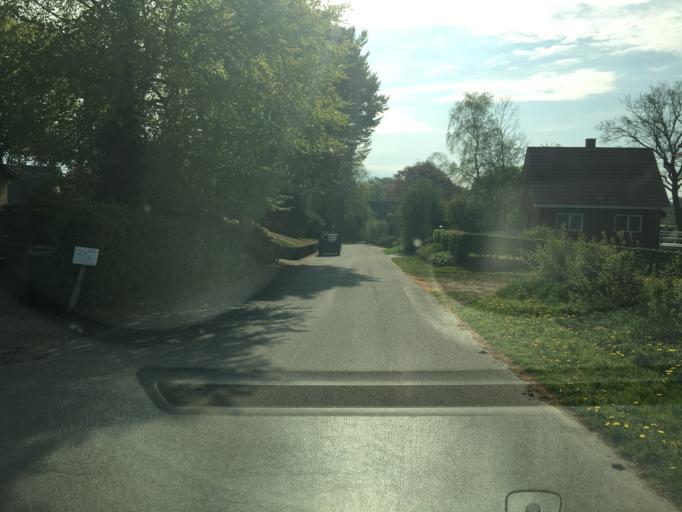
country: DK
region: South Denmark
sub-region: Haderslev Kommune
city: Vojens
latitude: 55.1877
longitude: 9.3833
